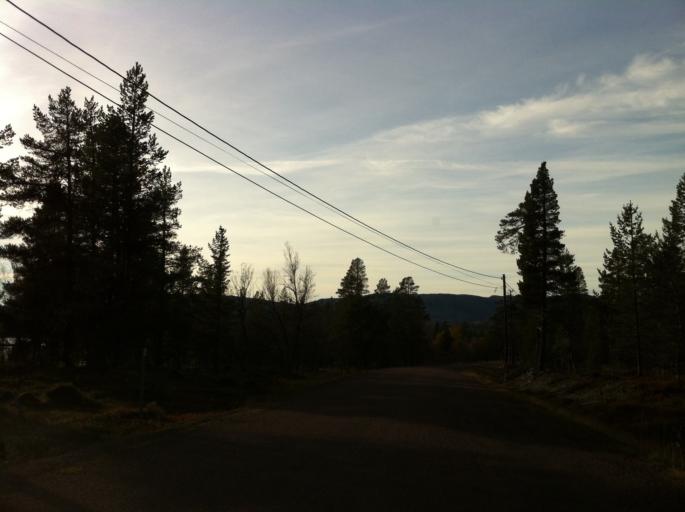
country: NO
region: Hedmark
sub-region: Engerdal
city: Engerdal
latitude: 62.0826
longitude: 12.1206
